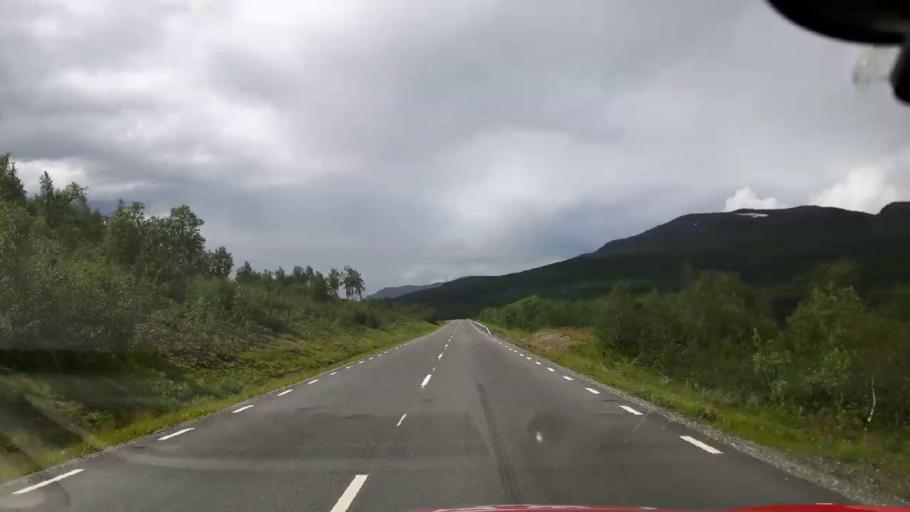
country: NO
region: Nordland
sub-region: Hattfjelldal
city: Hattfjelldal
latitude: 64.9907
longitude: 14.2224
